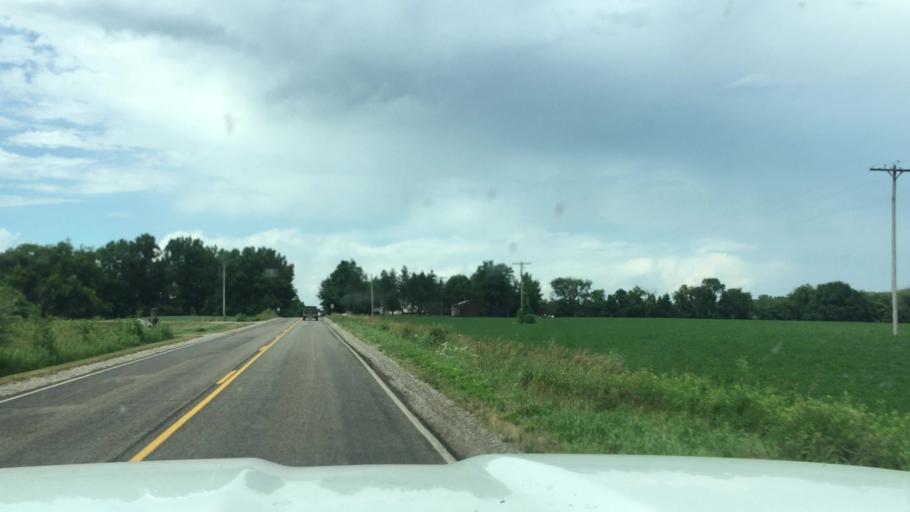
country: US
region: Michigan
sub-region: Montcalm County
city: Carson City
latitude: 43.2350
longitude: -84.7775
